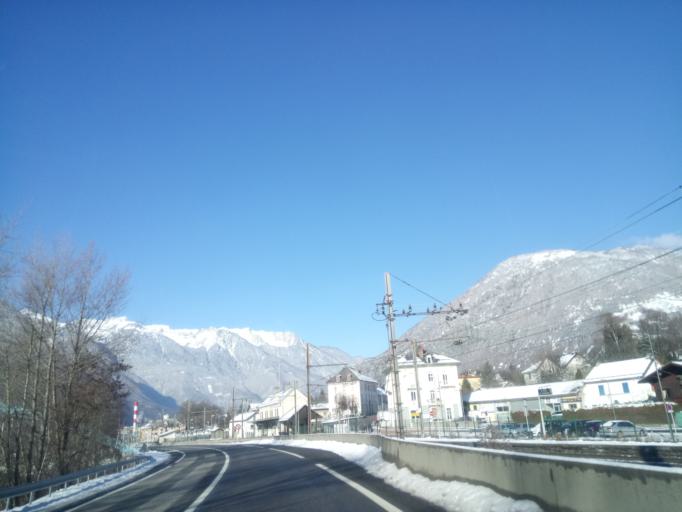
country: FR
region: Rhone-Alpes
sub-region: Departement de la Savoie
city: La Chambre
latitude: 45.3521
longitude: 6.3039
